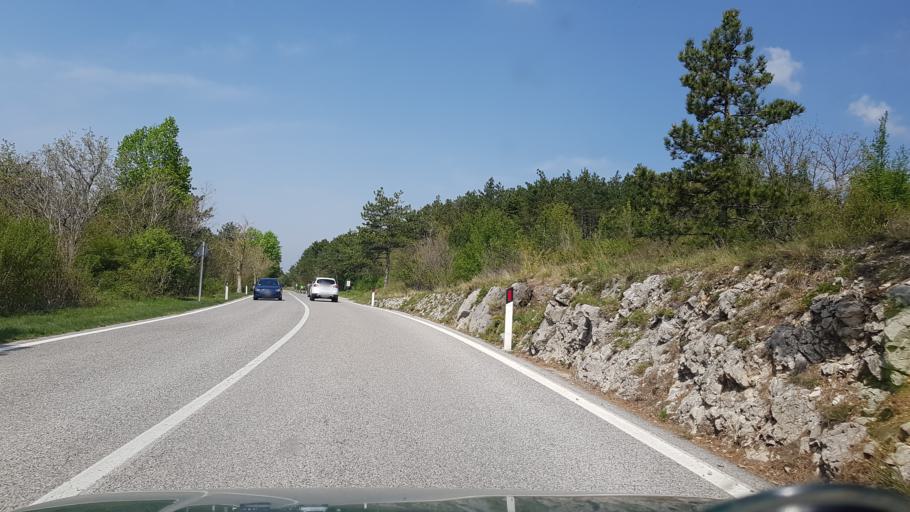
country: IT
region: Friuli Venezia Giulia
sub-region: Provincia di Trieste
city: Dolina
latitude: 45.6297
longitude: 13.8925
